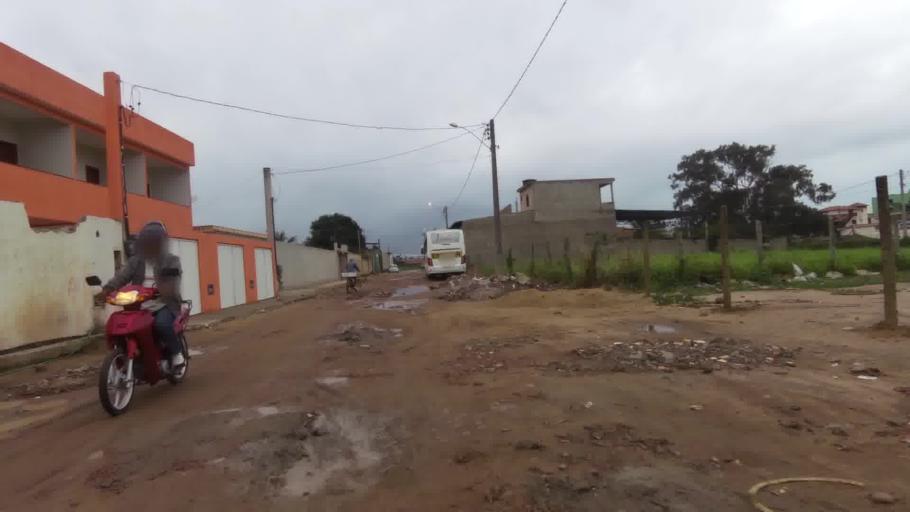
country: BR
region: Espirito Santo
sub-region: Marataizes
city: Marataizes
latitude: -21.0474
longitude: -40.8415
